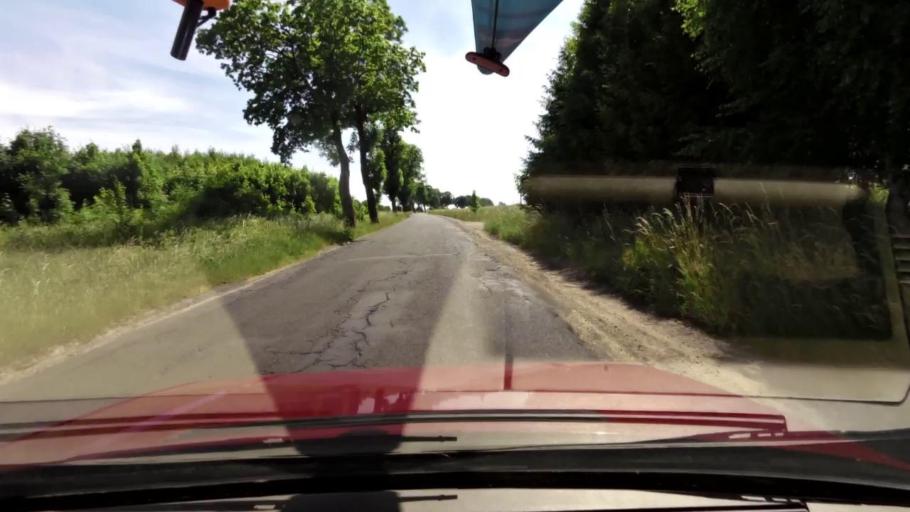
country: PL
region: Pomeranian Voivodeship
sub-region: Powiat slupski
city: Kobylnica
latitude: 54.4057
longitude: 17.0011
